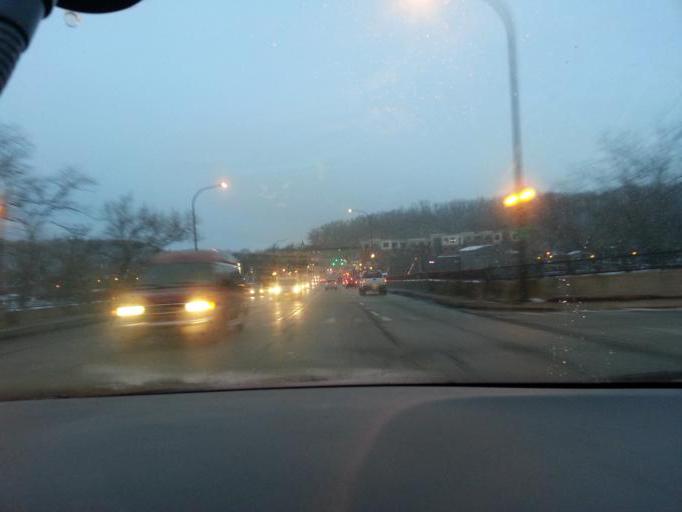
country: US
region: Illinois
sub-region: McHenry County
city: Algonquin
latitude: 42.1654
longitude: -88.2889
